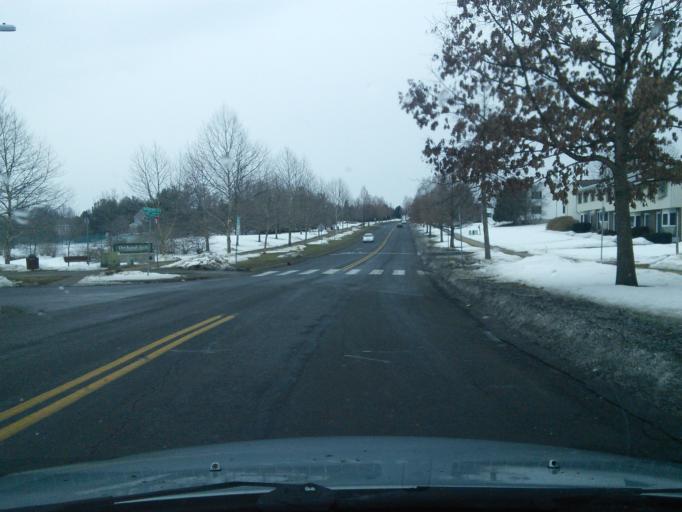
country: US
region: Pennsylvania
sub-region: Centre County
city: State College
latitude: 40.7724
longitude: -77.8665
